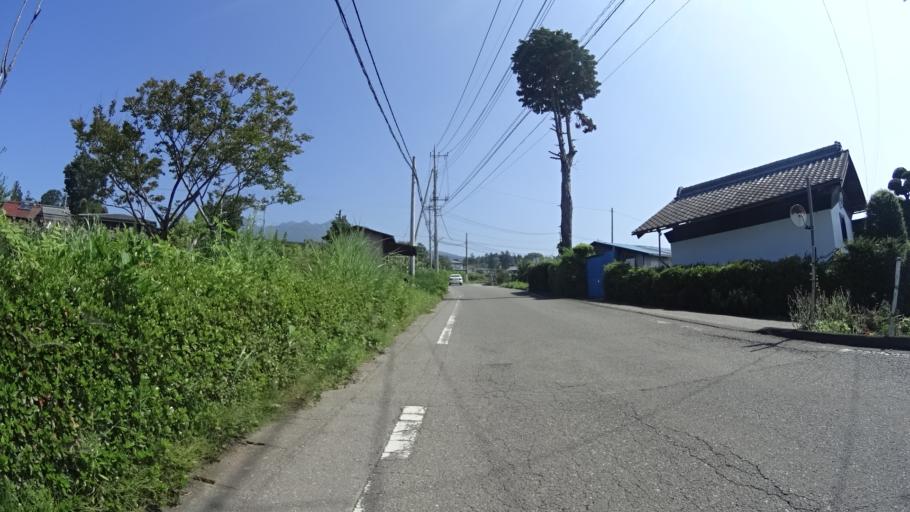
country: JP
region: Yamanashi
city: Nirasaki
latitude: 35.8767
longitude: 138.3510
